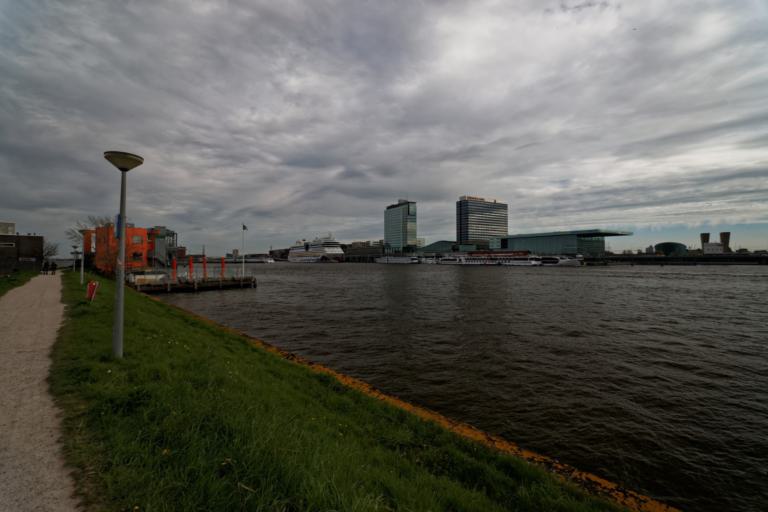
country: NL
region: North Holland
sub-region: Gemeente Amsterdam
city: Amsterdam
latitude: 52.3812
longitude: 4.9120
